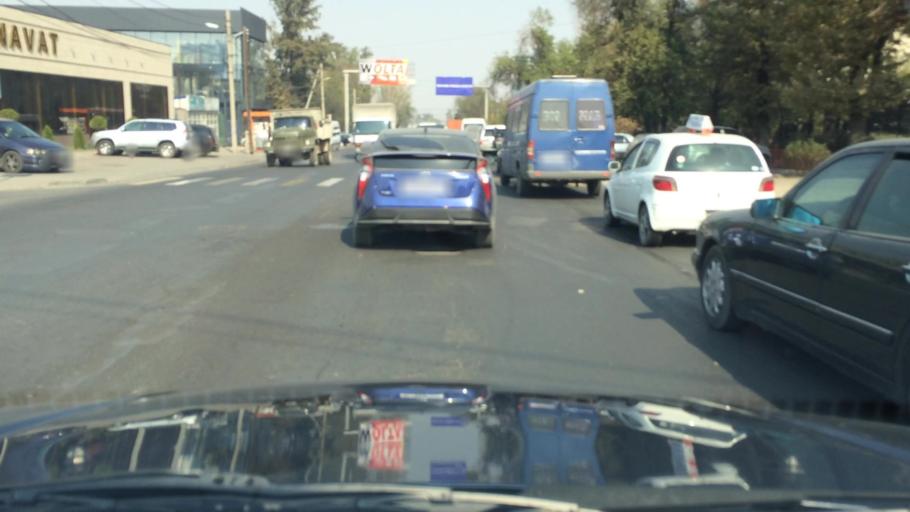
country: KG
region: Chuy
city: Lebedinovka
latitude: 42.8817
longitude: 74.6369
